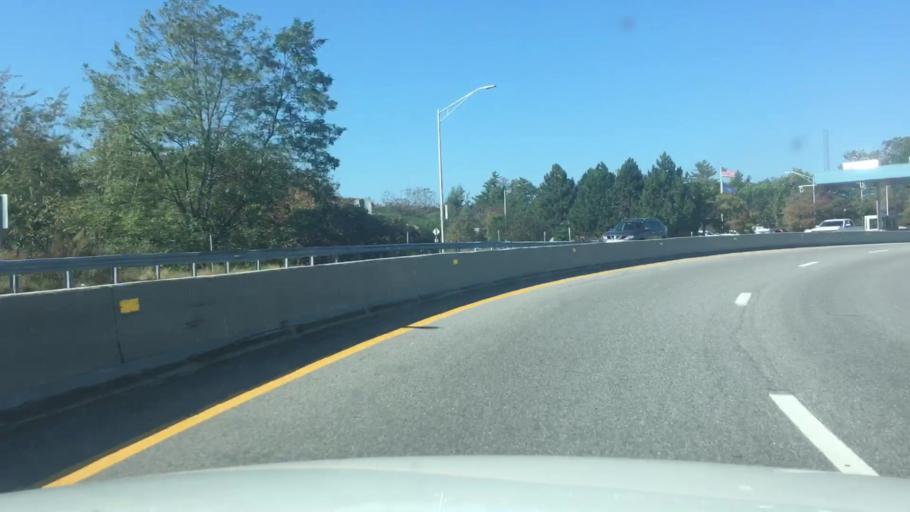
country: US
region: Maine
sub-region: Cumberland County
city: South Portland Gardens
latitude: 43.6483
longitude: -70.3344
